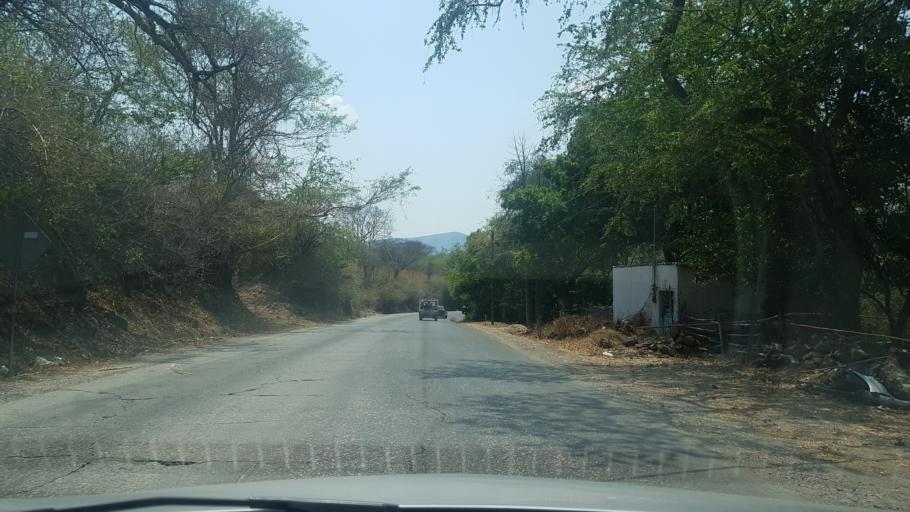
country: MX
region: Morelos
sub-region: Jiutepec
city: Independencia
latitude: 18.8042
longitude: -99.0918
